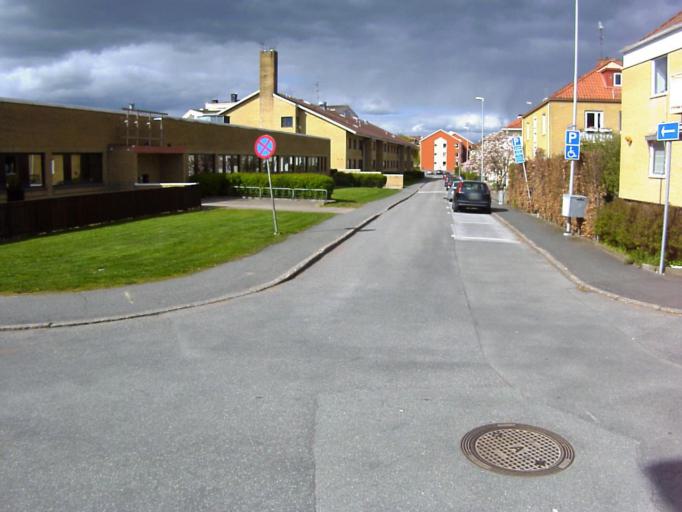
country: SE
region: Skane
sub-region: Kristianstads Kommun
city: Kristianstad
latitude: 56.0346
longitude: 14.1607
